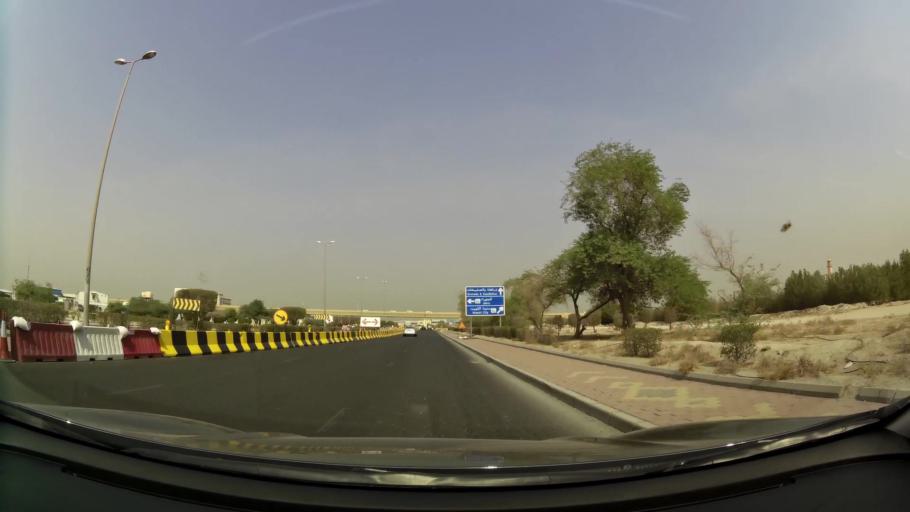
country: KW
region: Al Asimah
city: Ar Rabiyah
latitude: 29.3078
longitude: 47.8656
